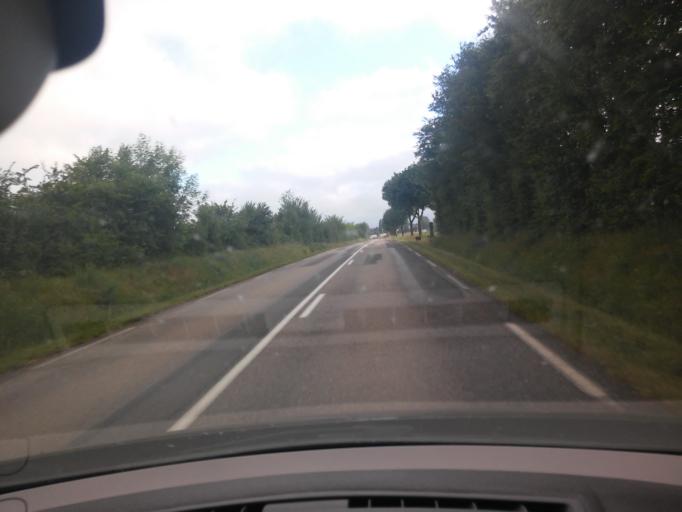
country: FR
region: Lorraine
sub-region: Departement de Meurthe-et-Moselle
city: Doncourt-les-Conflans
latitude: 49.0879
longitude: 5.8927
